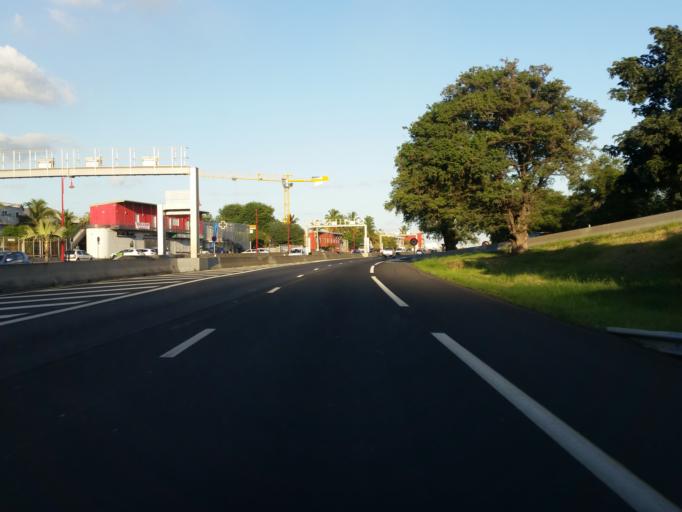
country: RE
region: Reunion
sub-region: Reunion
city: La Possession
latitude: -20.9230
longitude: 55.3435
